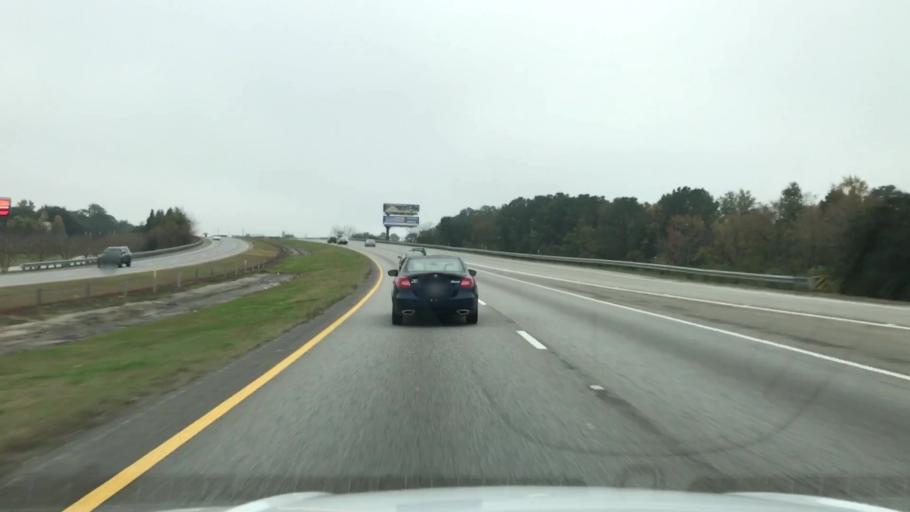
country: US
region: South Carolina
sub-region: Berkeley County
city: Hanahan
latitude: 32.8663
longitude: -80.0274
